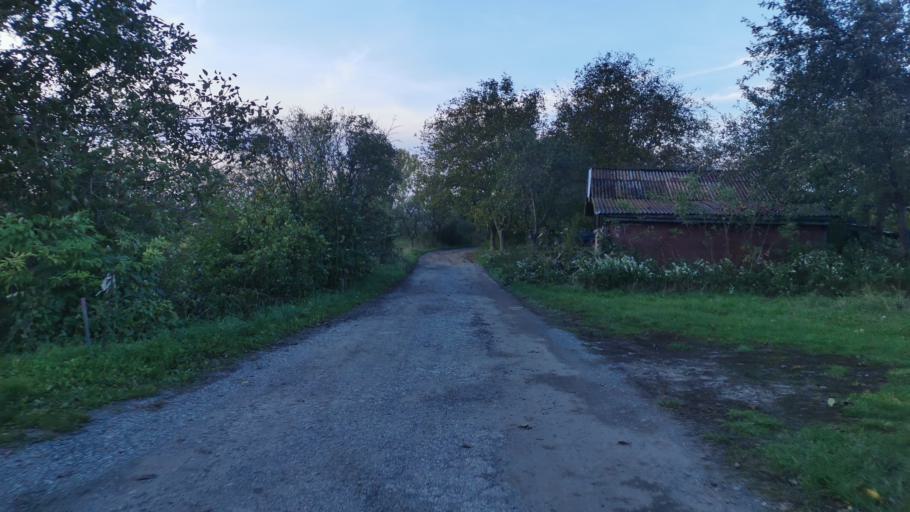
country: SK
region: Trnavsky
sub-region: Okres Skalica
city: Skalica
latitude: 48.8229
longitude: 17.2310
